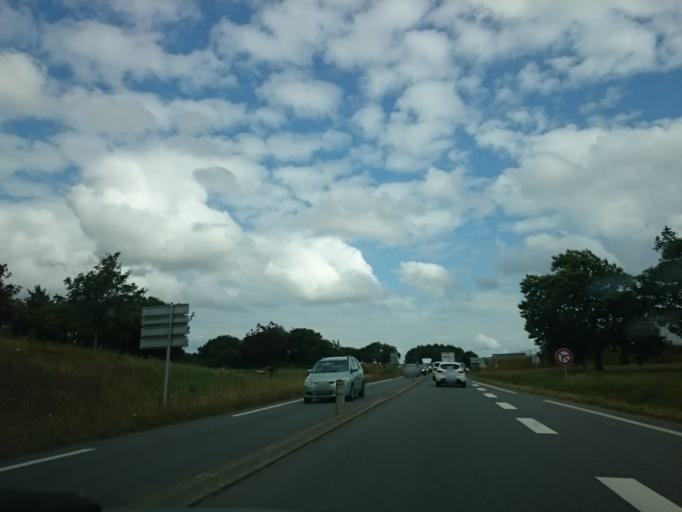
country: FR
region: Brittany
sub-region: Departement du Finistere
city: Gouesnou
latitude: 48.4335
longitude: -4.4425
